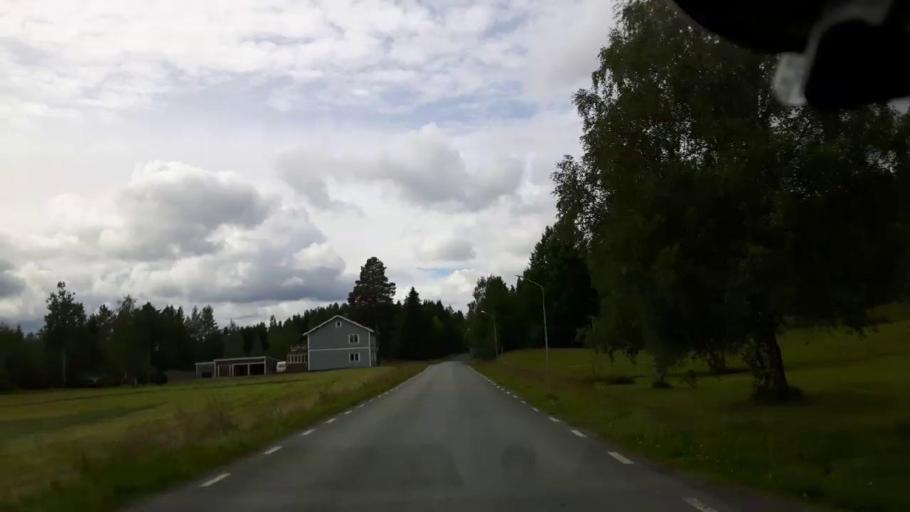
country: SE
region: Jaemtland
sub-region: Krokoms Kommun
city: Valla
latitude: 63.4869
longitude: 14.0134
